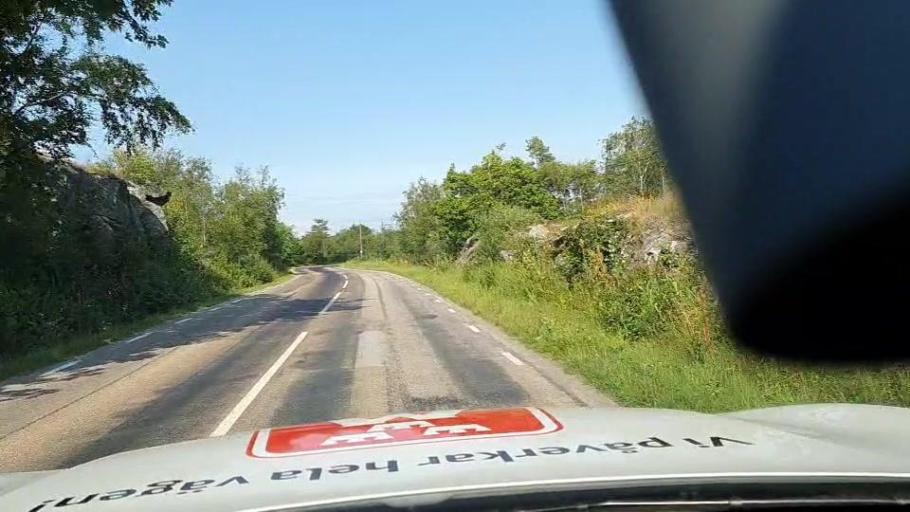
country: SE
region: Vaestra Goetaland
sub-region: Tjorns Kommun
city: Skaerhamn
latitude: 58.0918
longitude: 11.4867
